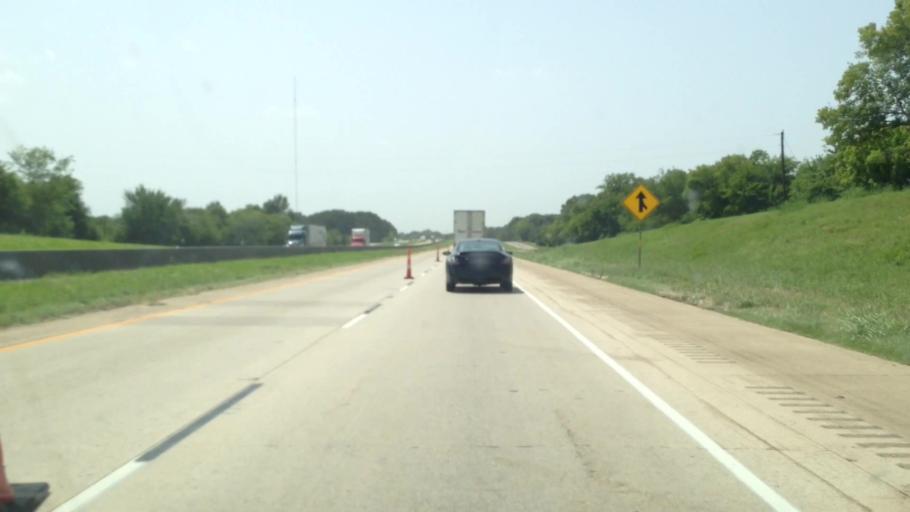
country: US
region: Texas
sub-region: Hopkins County
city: Sulphur Springs
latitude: 33.1238
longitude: -95.7345
